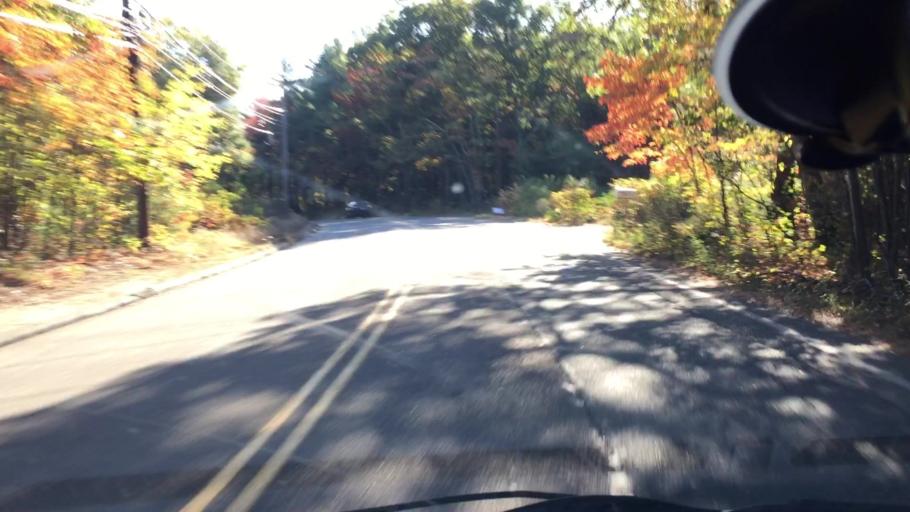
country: US
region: Massachusetts
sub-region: Norfolk County
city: Westwood
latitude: 42.2028
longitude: -71.2546
